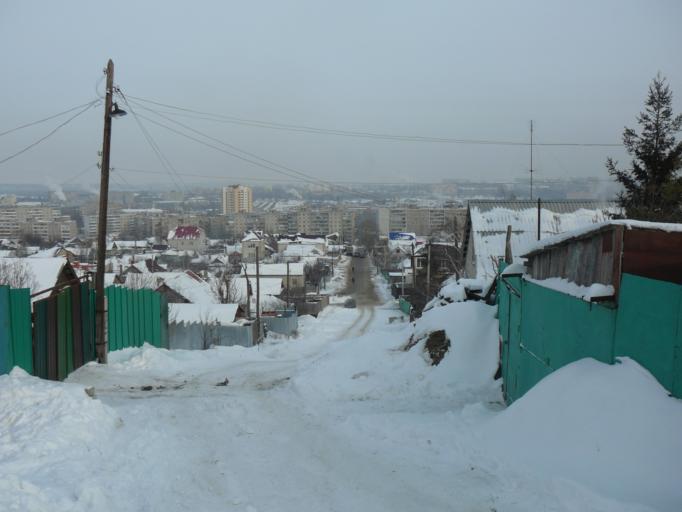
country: RU
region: Saratov
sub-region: Saratovskiy Rayon
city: Saratov
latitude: 51.5576
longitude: 45.9820
